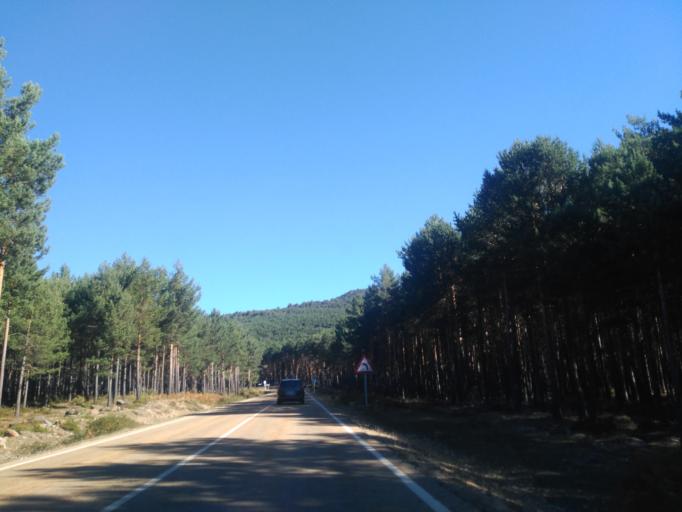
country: ES
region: Castille and Leon
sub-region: Provincia de Soria
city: Vinuesa
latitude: 41.9737
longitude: -2.7863
